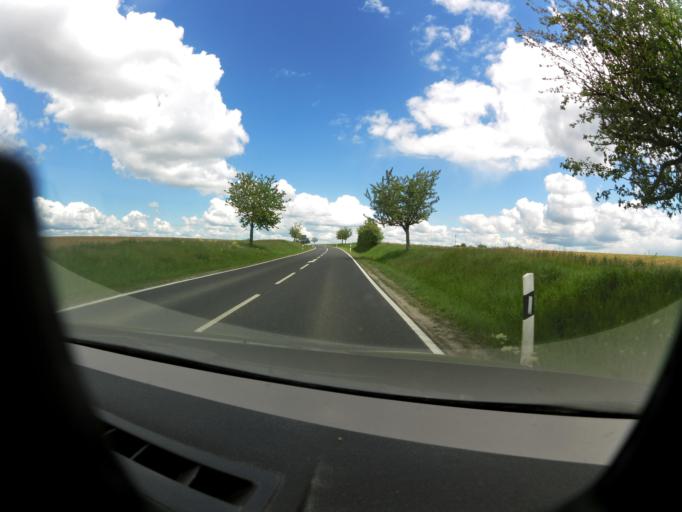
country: DE
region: Bavaria
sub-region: Regierungsbezirk Unterfranken
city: Waigolshausen
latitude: 49.9465
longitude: 10.1428
